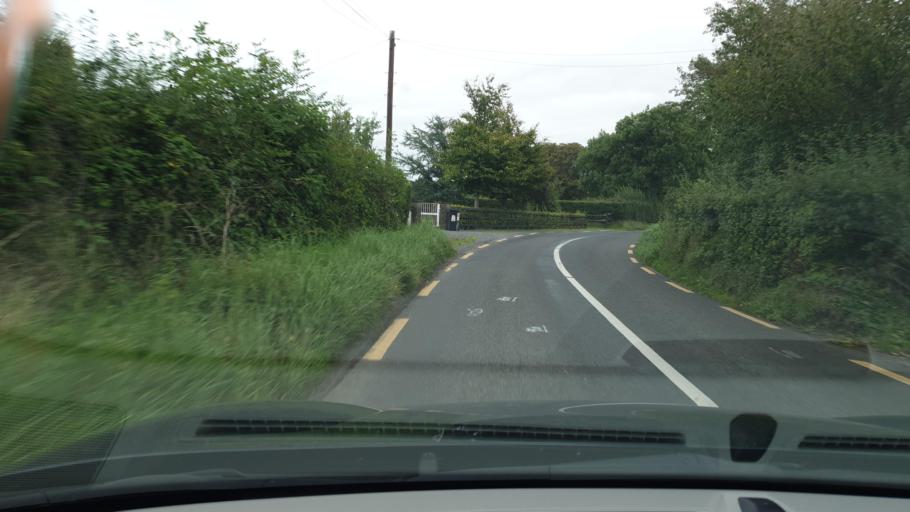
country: IE
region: Leinster
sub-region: Kildare
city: Kilcock
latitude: 53.4110
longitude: -6.6639
